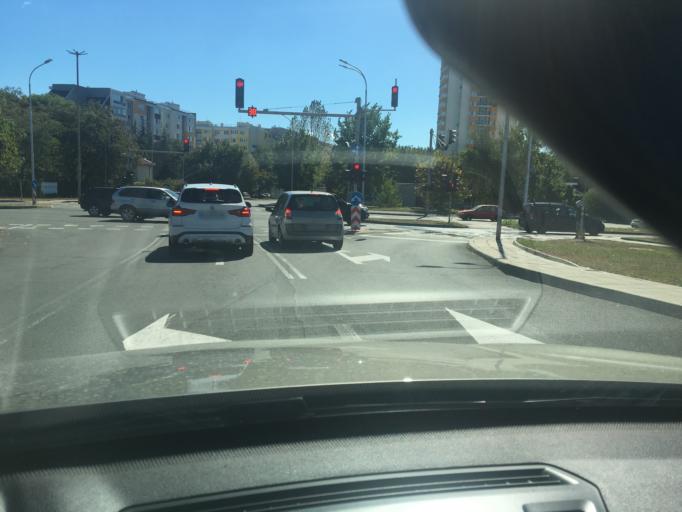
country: BG
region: Burgas
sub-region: Obshtina Burgas
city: Burgas
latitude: 42.5313
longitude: 27.4621
